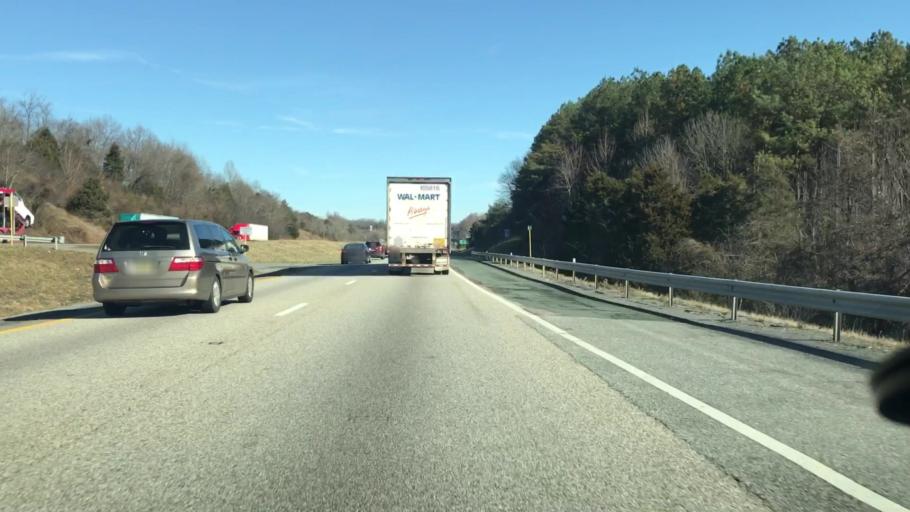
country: US
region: Virginia
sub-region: Rockbridge County
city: Glasgow
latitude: 37.6354
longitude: -79.5661
